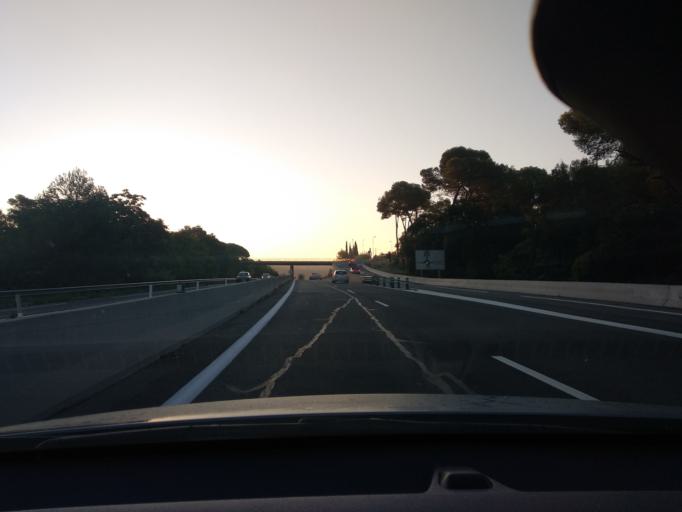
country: FR
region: Provence-Alpes-Cote d'Azur
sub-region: Departement des Alpes-Maritimes
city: Grasse
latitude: 43.6374
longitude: 6.9387
